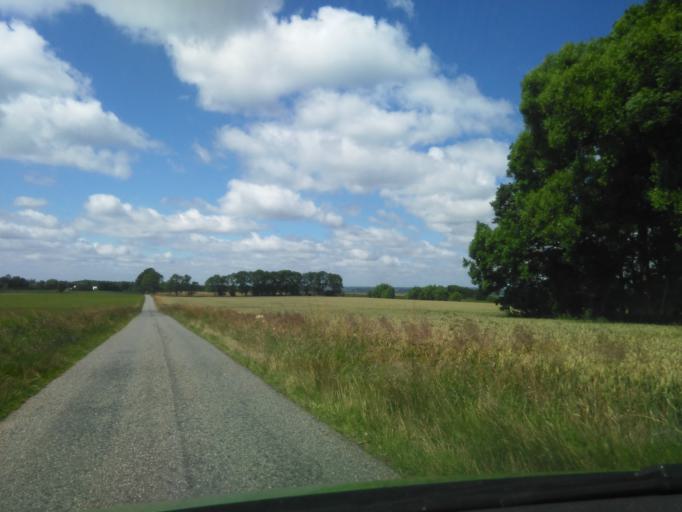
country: DK
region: Central Jutland
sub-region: Arhus Kommune
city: Logten
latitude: 56.1966
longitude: 10.3748
